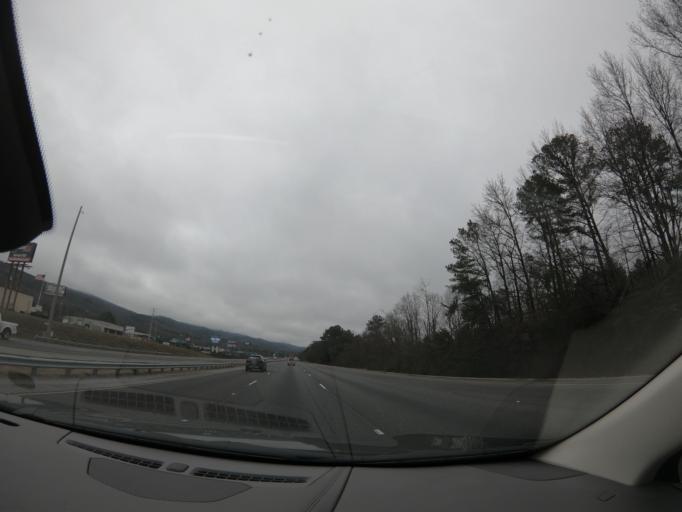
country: US
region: Georgia
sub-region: Whitfield County
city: Dalton
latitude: 34.6915
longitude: -85.0030
